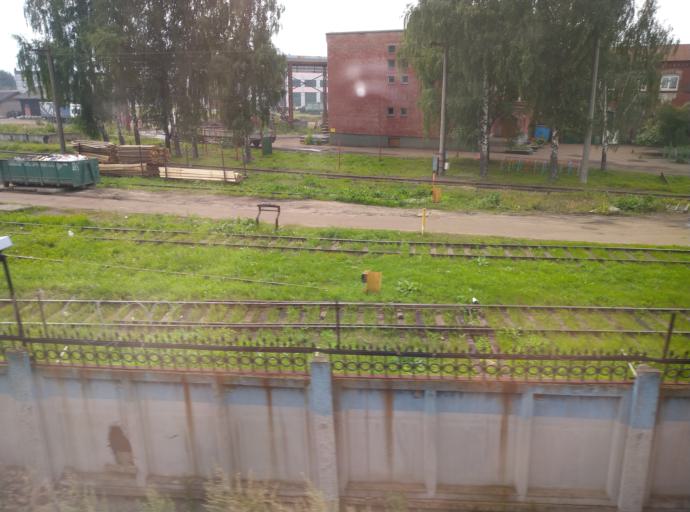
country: RU
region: Jaroslavl
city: Yaroslavl
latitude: 57.6004
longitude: 39.8894
